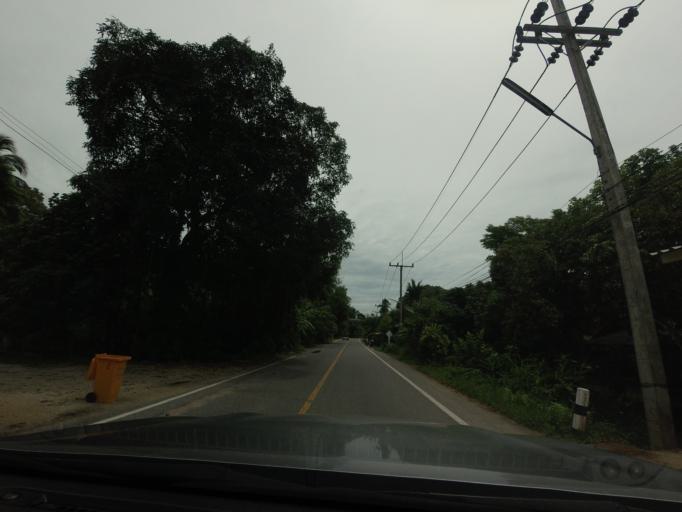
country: TH
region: Pattani
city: Kapho
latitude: 6.6398
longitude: 101.5503
